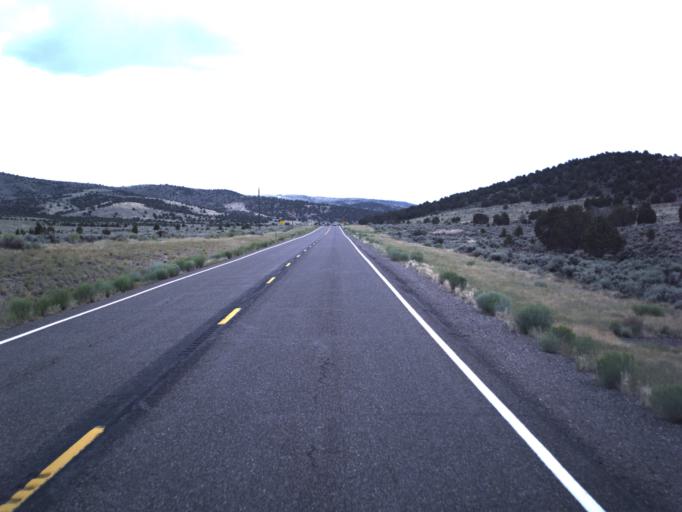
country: US
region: Utah
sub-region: Wayne County
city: Loa
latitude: 38.5588
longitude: -111.8378
